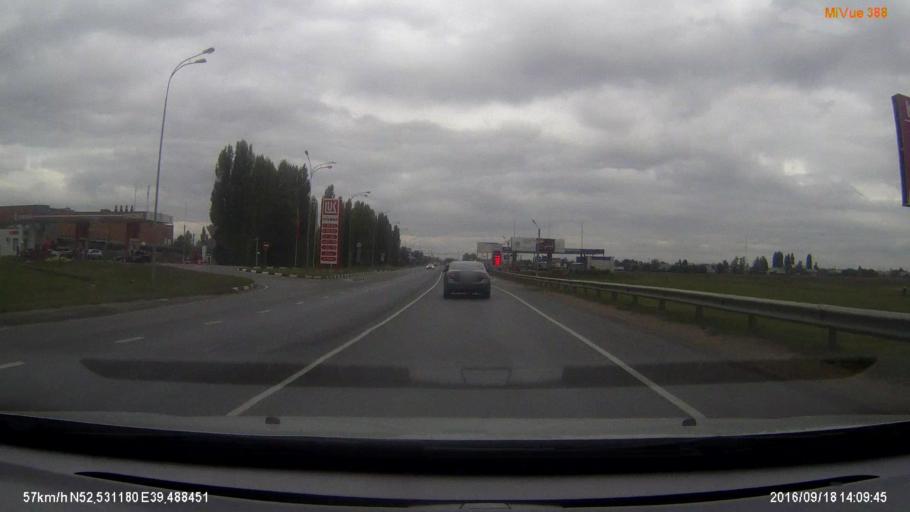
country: RU
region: Lipetsk
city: Syrskoye
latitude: 52.5932
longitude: 39.5212
